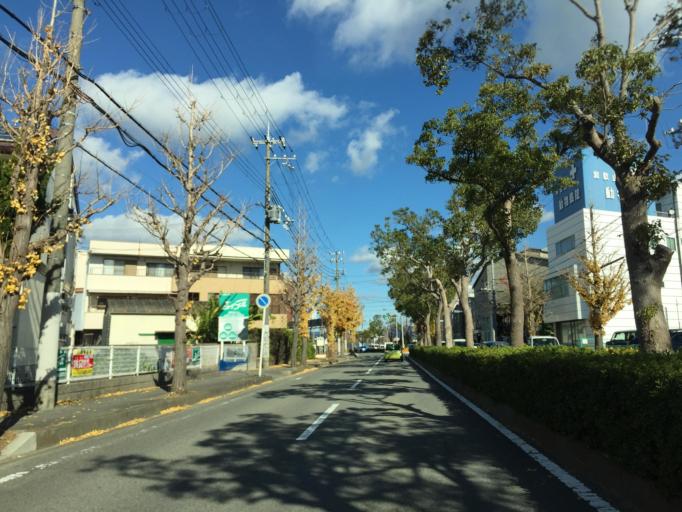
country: JP
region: Wakayama
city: Wakayama-shi
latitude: 34.2029
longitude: 135.1791
